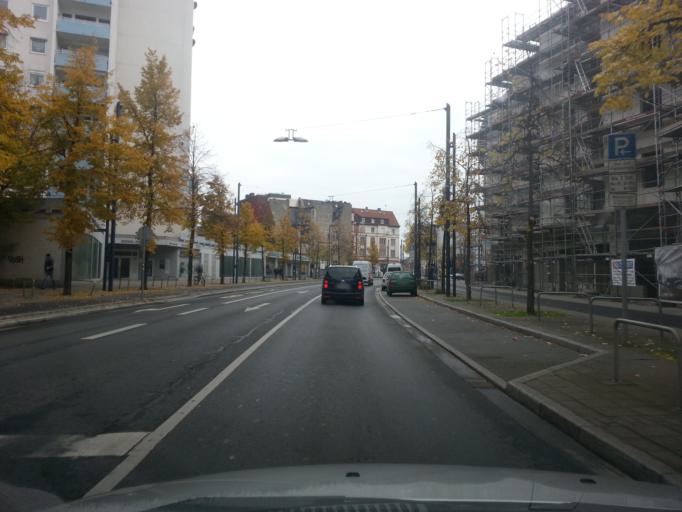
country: DE
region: Hesse
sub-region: Regierungsbezirk Darmstadt
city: Offenbach
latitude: 50.1050
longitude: 8.7676
